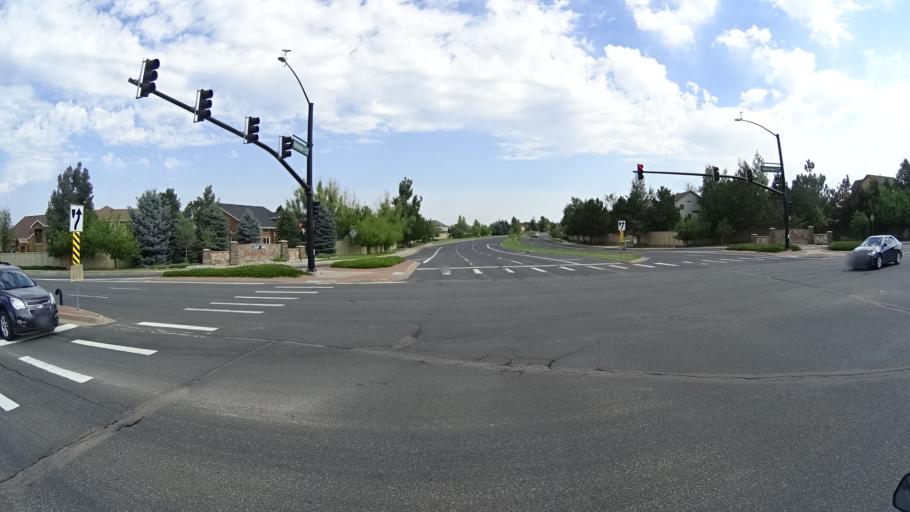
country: US
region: Colorado
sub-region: El Paso County
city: Cimarron Hills
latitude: 38.9123
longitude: -104.6951
